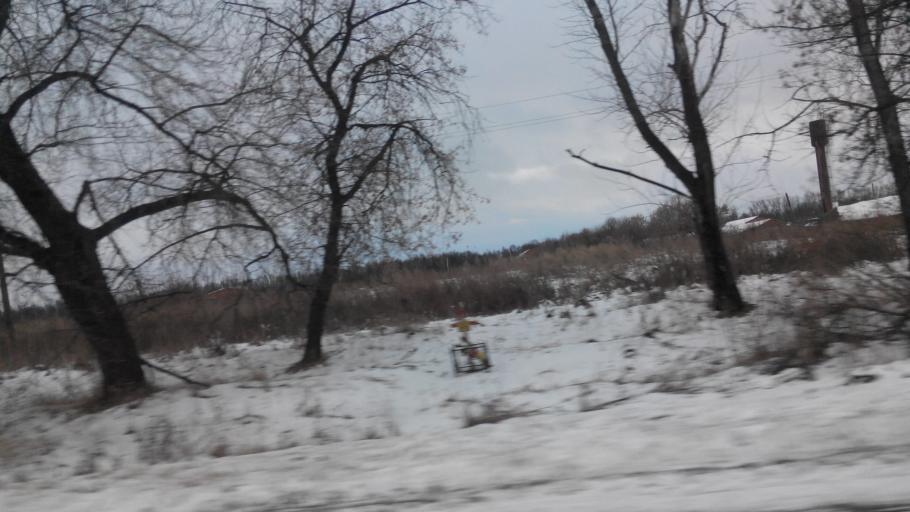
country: RU
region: Tula
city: Podlesnyy
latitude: 53.9650
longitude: 38.2706
